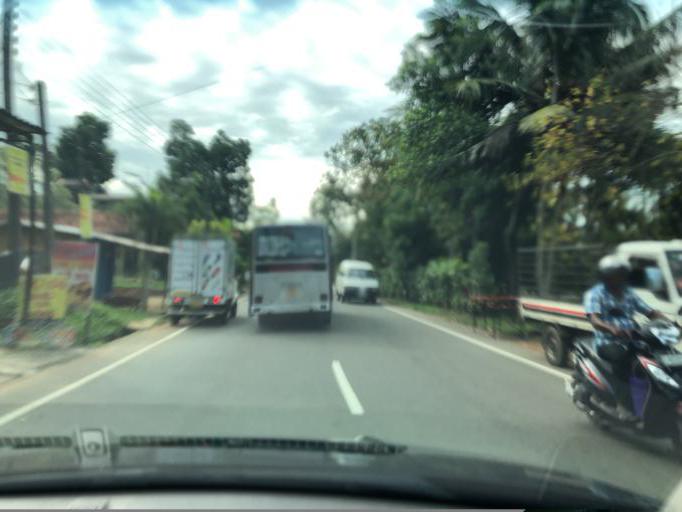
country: LK
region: Western
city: Kalutara
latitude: 6.5615
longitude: 80.0085
